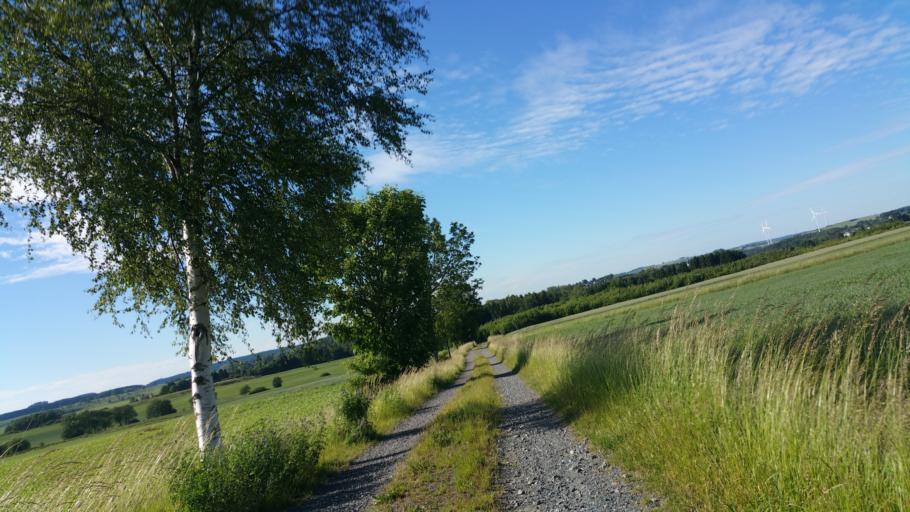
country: DE
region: Bavaria
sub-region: Upper Franconia
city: Schwarzenbach an der Saale
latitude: 50.2060
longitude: 11.9280
